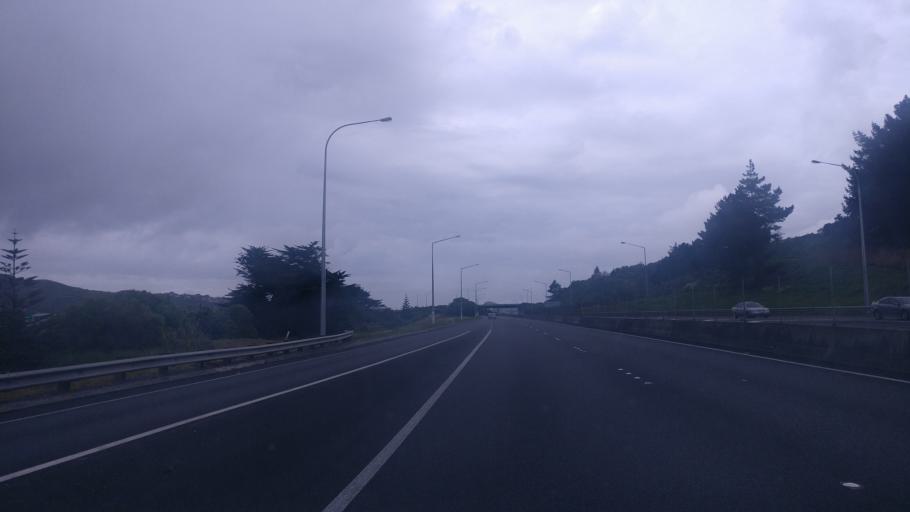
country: NZ
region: Wellington
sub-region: Porirua City
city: Porirua
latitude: -41.1361
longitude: 174.8448
